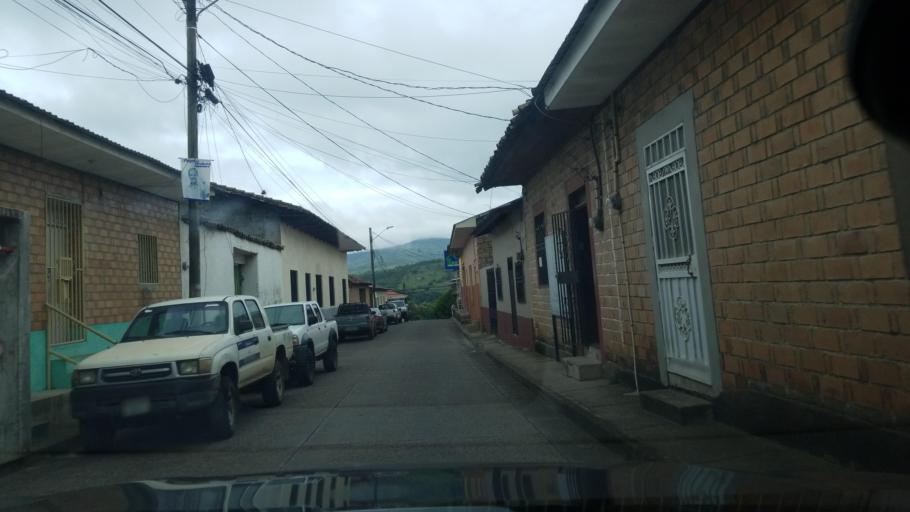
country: HN
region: Choluteca
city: San Marcos de Colon
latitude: 13.4320
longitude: -86.8097
